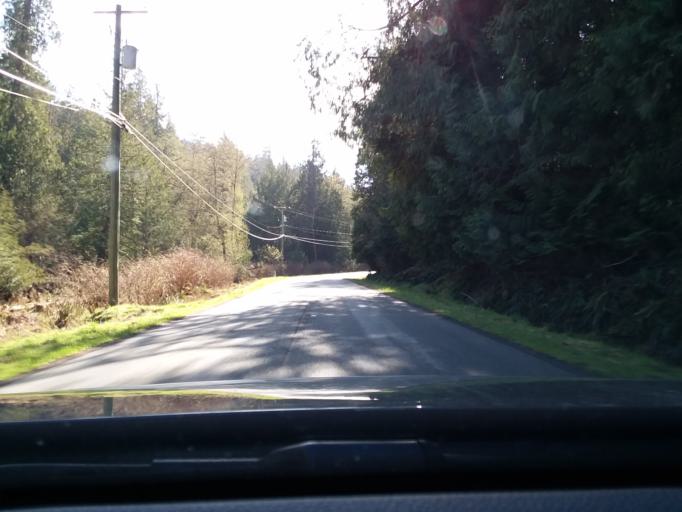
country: CA
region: British Columbia
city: North Cowichan
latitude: 48.9279
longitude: -123.4576
